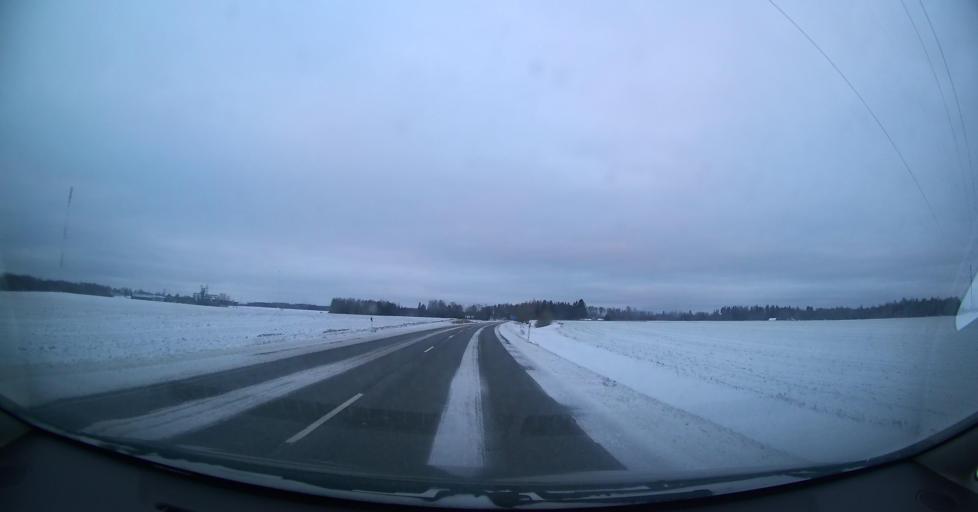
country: EE
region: Harju
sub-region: Anija vald
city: Kehra
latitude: 59.2569
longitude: 25.3354
